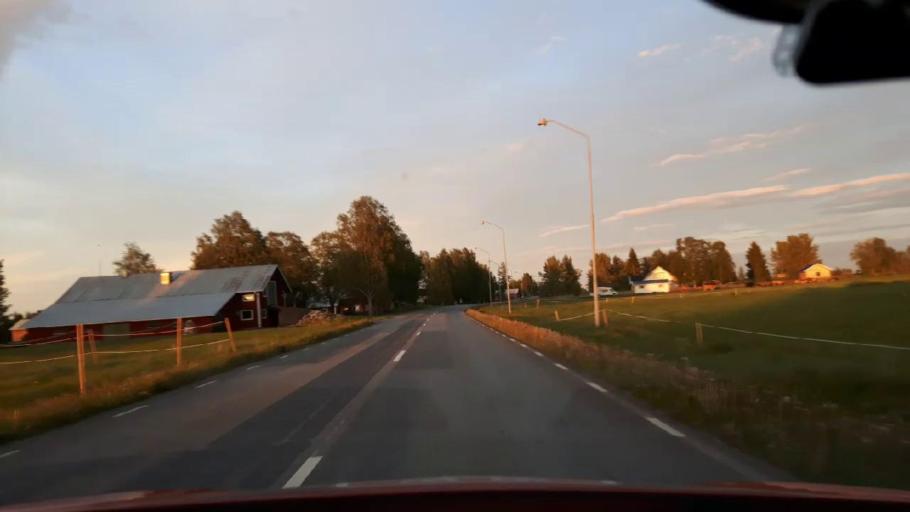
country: SE
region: Jaemtland
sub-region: OEstersunds Kommun
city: Ostersund
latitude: 63.1215
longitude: 14.7107
